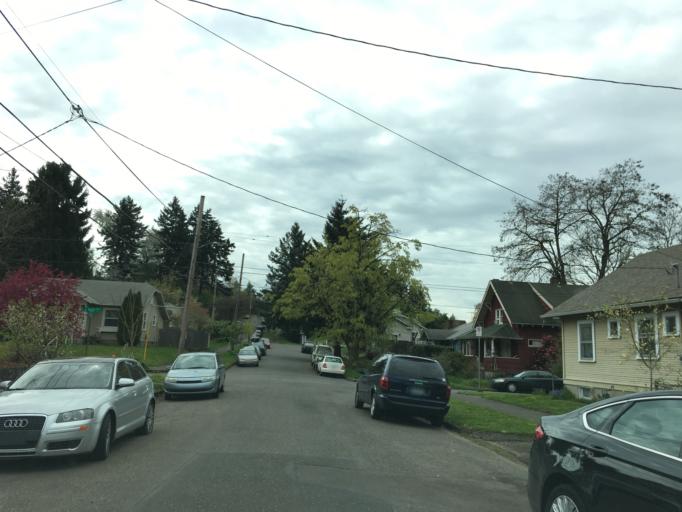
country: US
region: Oregon
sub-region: Multnomah County
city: Lents
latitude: 45.5276
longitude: -122.5997
